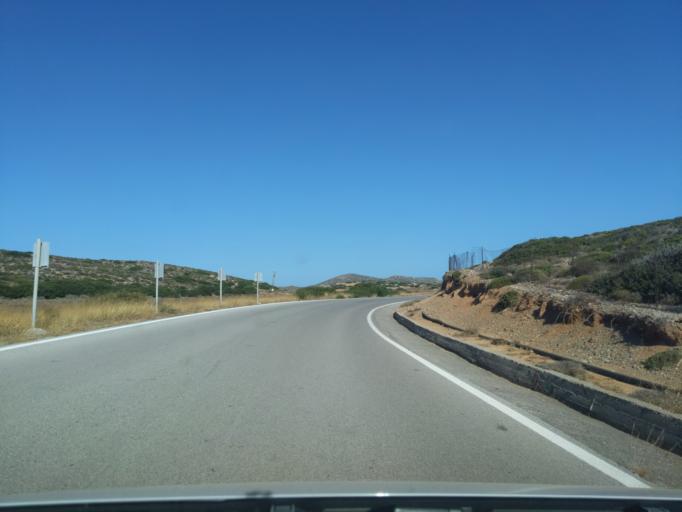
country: GR
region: Crete
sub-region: Nomos Lasithiou
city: Palekastro
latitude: 35.2378
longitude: 26.2490
